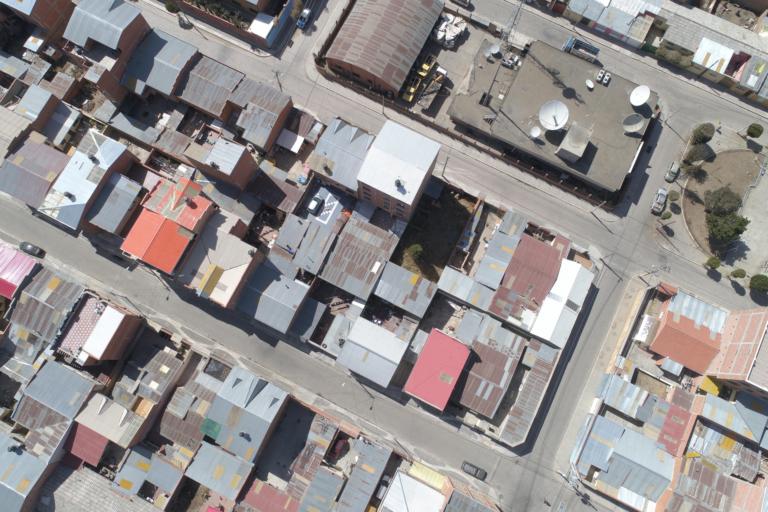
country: BO
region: La Paz
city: La Paz
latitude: -16.5267
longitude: -68.1569
